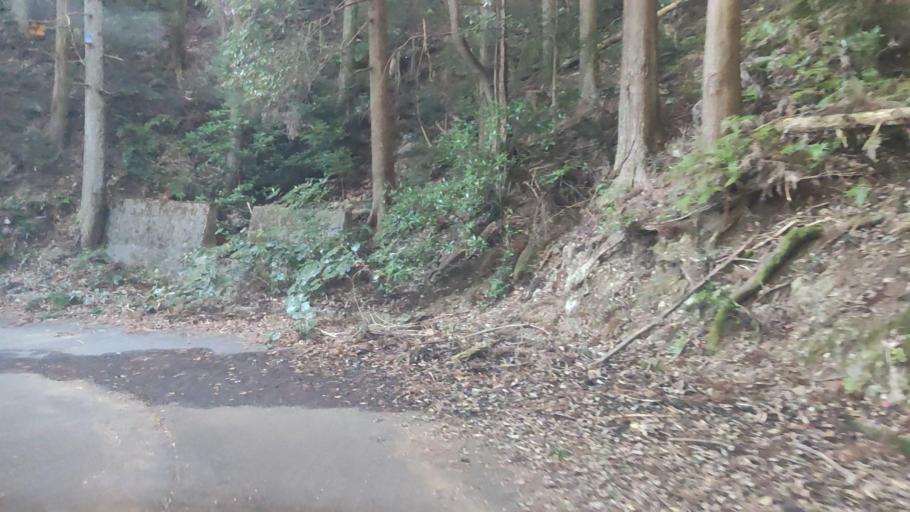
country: JP
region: Oita
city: Saiki
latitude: 32.7853
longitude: 131.8566
